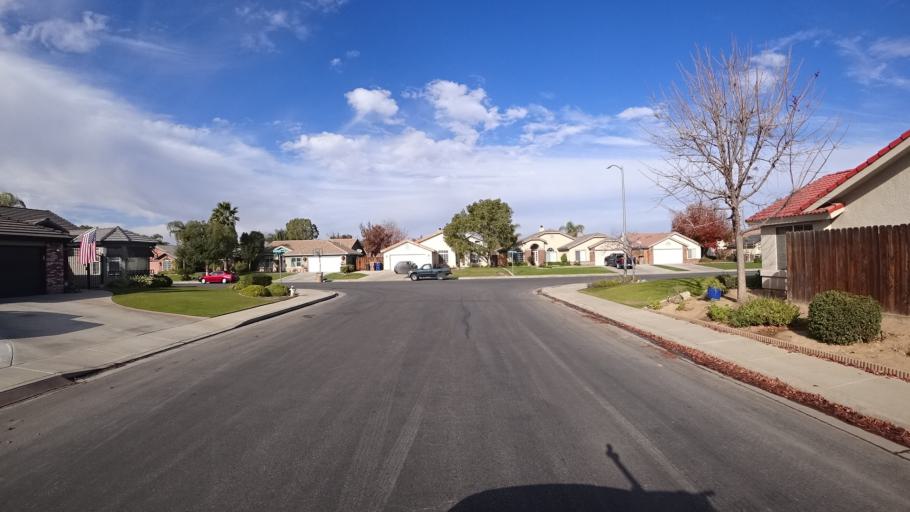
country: US
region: California
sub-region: Kern County
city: Greenacres
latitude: 35.3999
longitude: -119.1244
